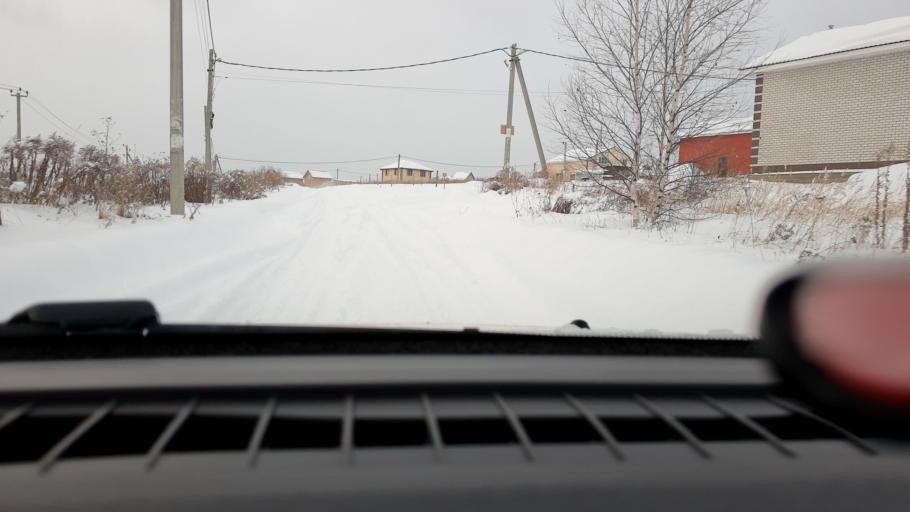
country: RU
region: Nizjnij Novgorod
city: Afonino
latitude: 56.1277
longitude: 43.9964
